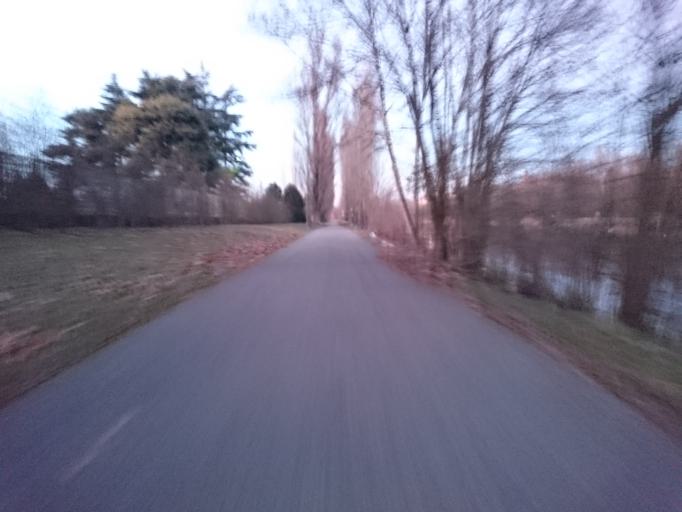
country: IT
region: Veneto
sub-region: Provincia di Verona
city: Salionze
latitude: 45.3998
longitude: 10.7167
